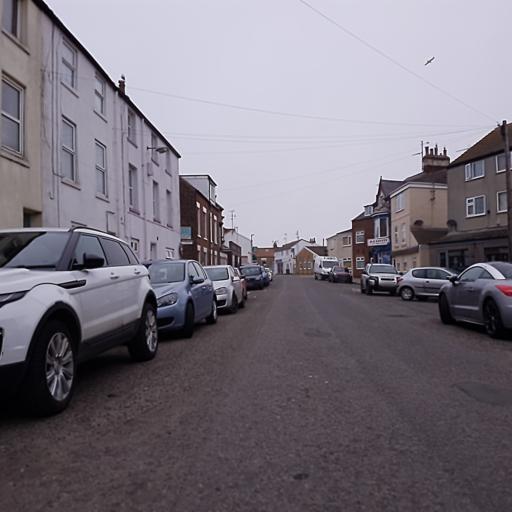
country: GB
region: England
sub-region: North Yorkshire
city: Filey
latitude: 54.2107
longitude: -0.2885
